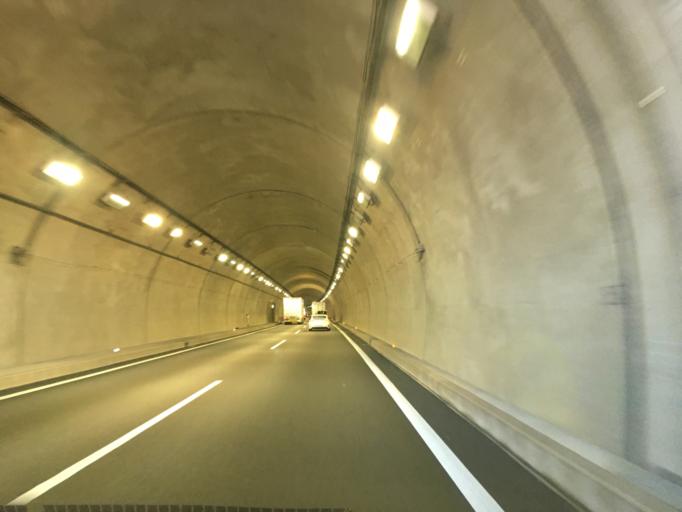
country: JP
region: Kanagawa
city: Zama
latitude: 35.5143
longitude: 139.3609
